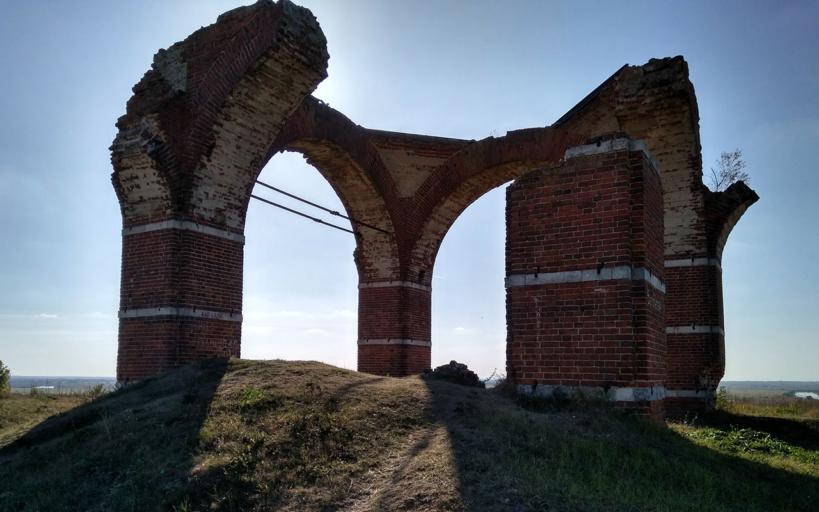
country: RU
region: Rjazan
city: Spassk-Ryazanskiy
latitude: 54.3968
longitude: 40.4224
